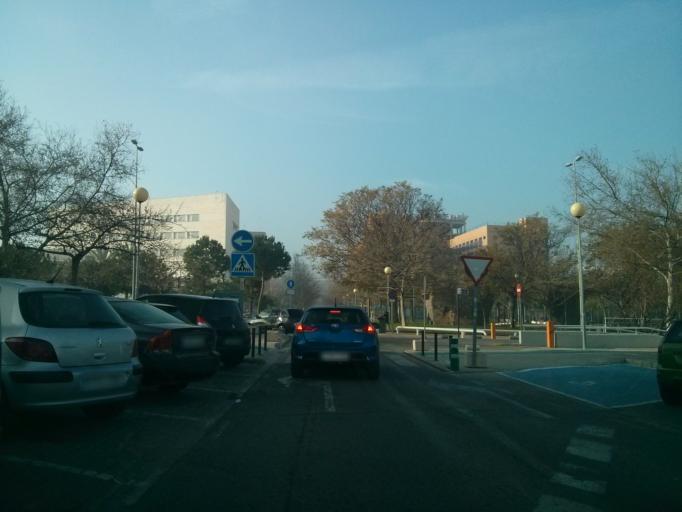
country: ES
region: Valencia
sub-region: Provincia de Valencia
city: Alboraya
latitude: 39.4808
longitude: -0.3392
